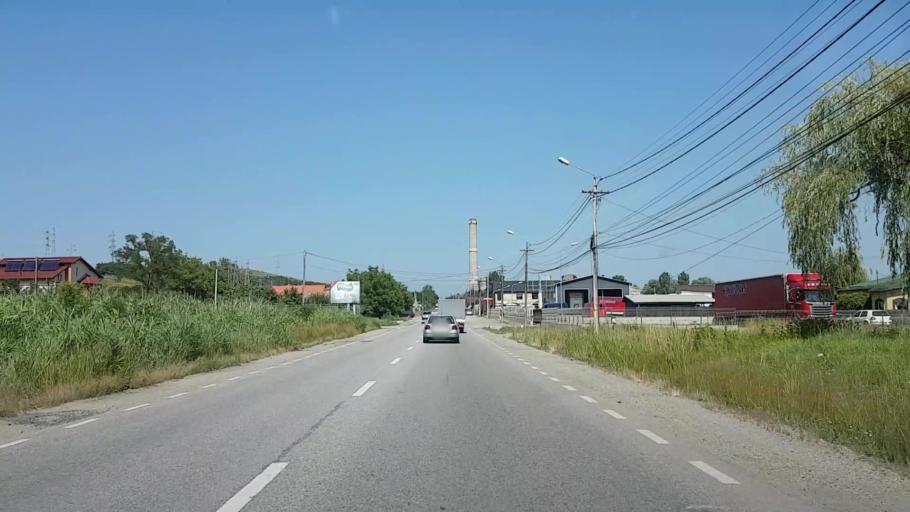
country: RO
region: Cluj
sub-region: Municipiul Dej
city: Dej
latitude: 47.1582
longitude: 23.8864
